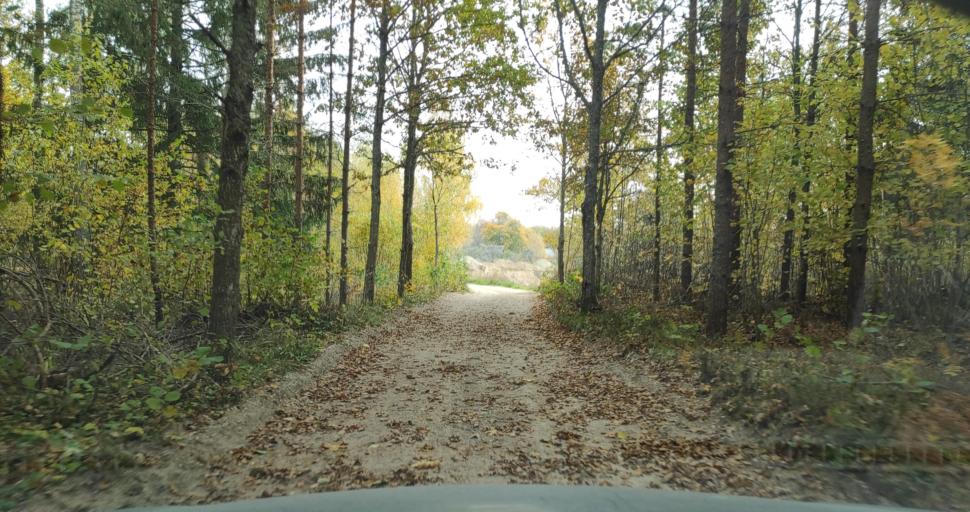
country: LV
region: Alsunga
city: Alsunga
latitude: 57.0383
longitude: 21.7000
